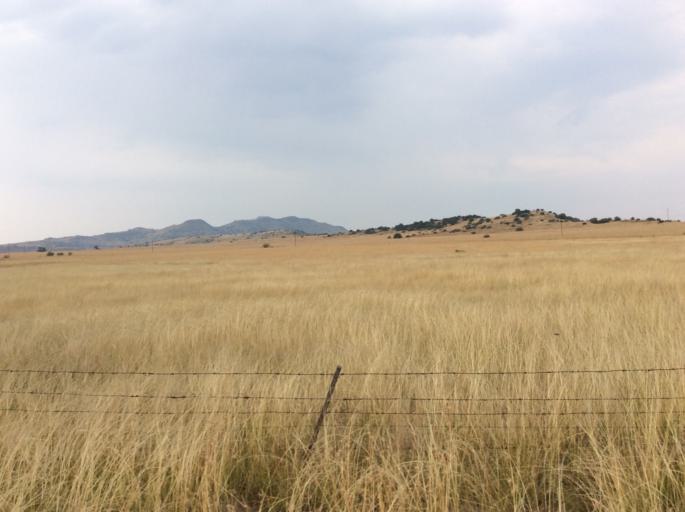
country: LS
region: Mafeteng
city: Mafeteng
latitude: -29.9908
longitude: 27.0187
